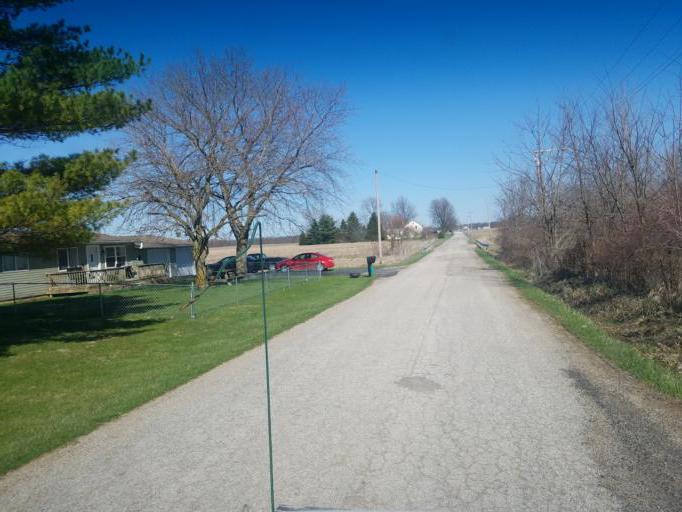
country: US
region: Ohio
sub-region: Morrow County
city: Mount Gilead
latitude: 40.5866
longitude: -82.8996
